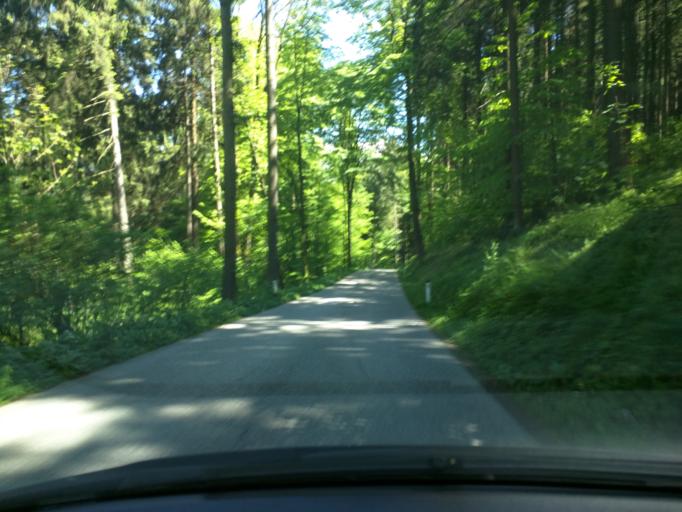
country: AT
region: Lower Austria
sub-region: Politischer Bezirk Melk
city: Blindenmarkt
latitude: 48.1586
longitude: 14.9741
